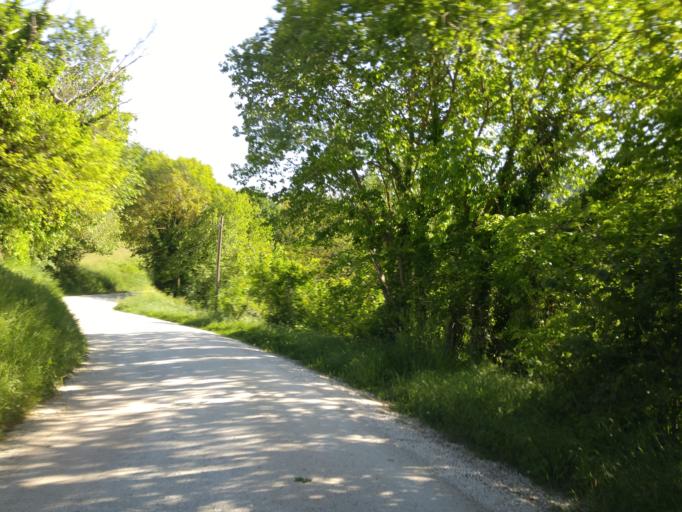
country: IT
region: The Marches
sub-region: Provincia di Pesaro e Urbino
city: Mombaroccio
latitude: 43.8214
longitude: 12.8415
